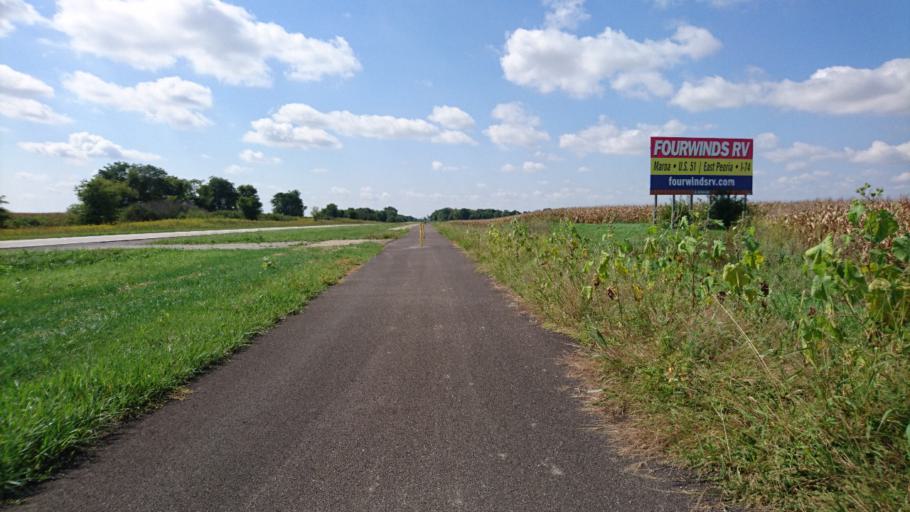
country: US
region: Illinois
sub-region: McLean County
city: Lexington
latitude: 40.5873
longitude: -88.8640
